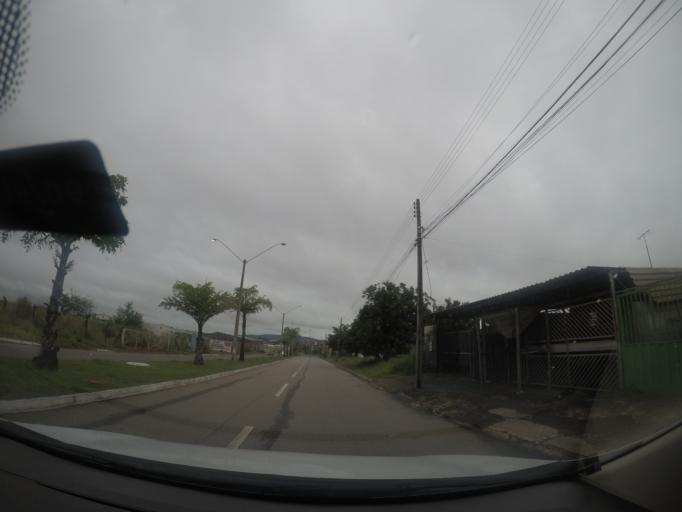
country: BR
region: Goias
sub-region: Goiania
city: Goiania
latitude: -16.7521
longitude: -49.3220
